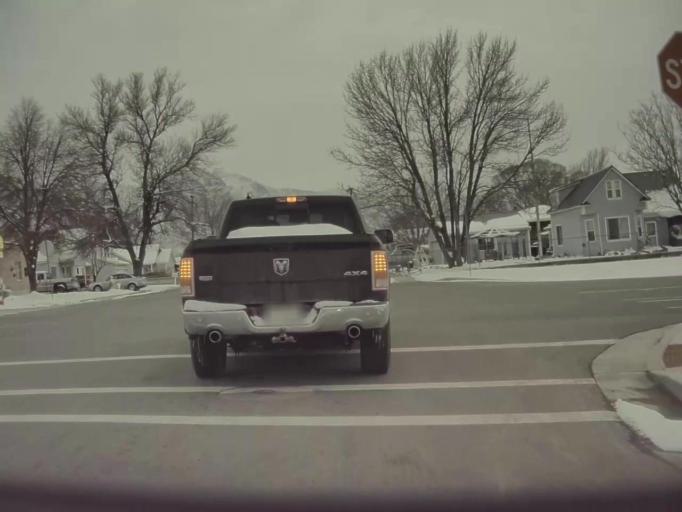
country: US
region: Utah
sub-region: Utah County
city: Spanish Fork
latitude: 40.1100
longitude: -111.6390
